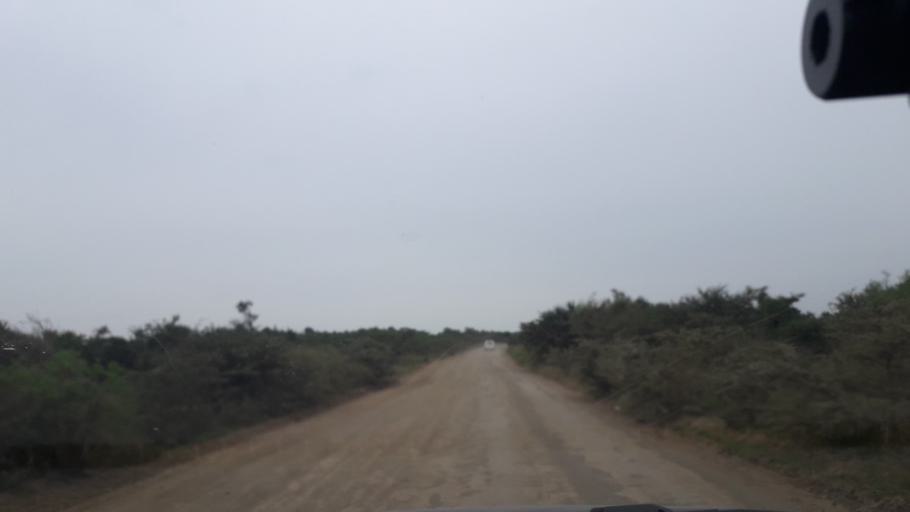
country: ZA
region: Eastern Cape
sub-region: Buffalo City Metropolitan Municipality
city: Bhisho
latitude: -32.7910
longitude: 27.3334
